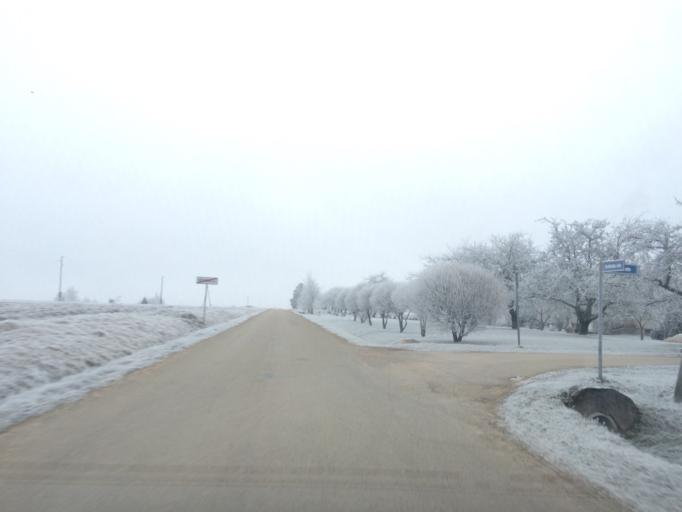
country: LV
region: Ludzas Rajons
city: Ludza
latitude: 56.6333
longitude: 27.5212
